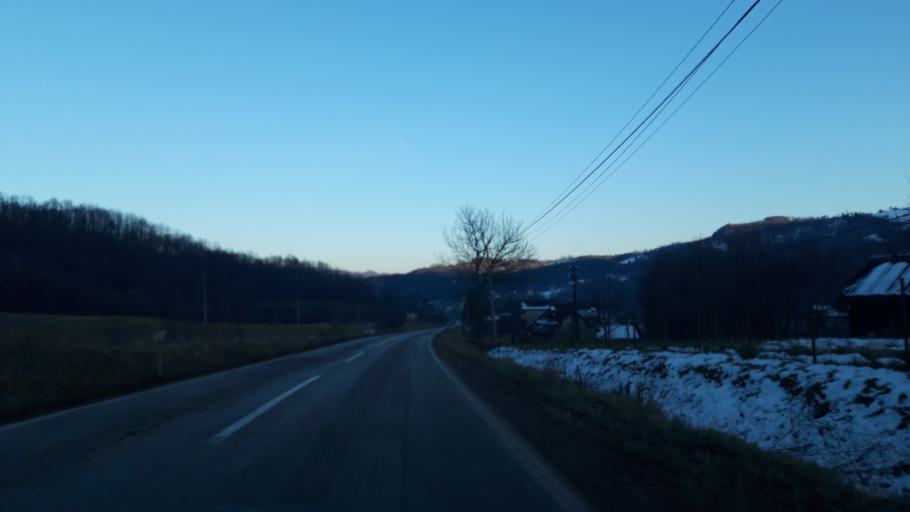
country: BA
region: Republika Srpska
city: Milici
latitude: 44.1645
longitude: 19.0554
